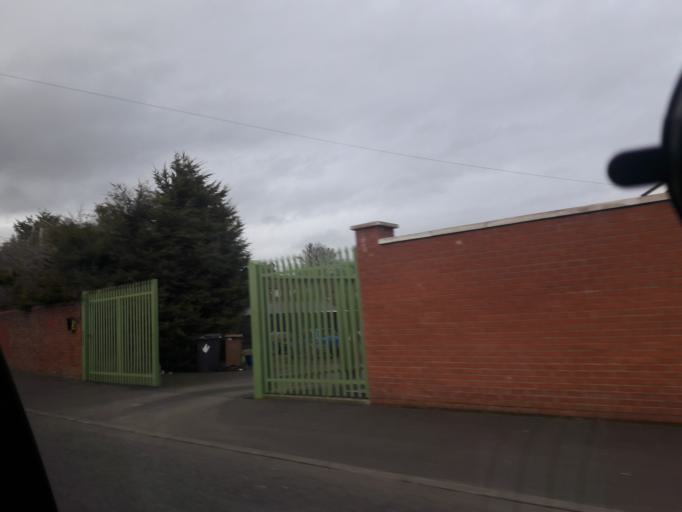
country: GB
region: Northern Ireland
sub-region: City of Belfast
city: Belfast
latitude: 54.6263
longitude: -5.9410
